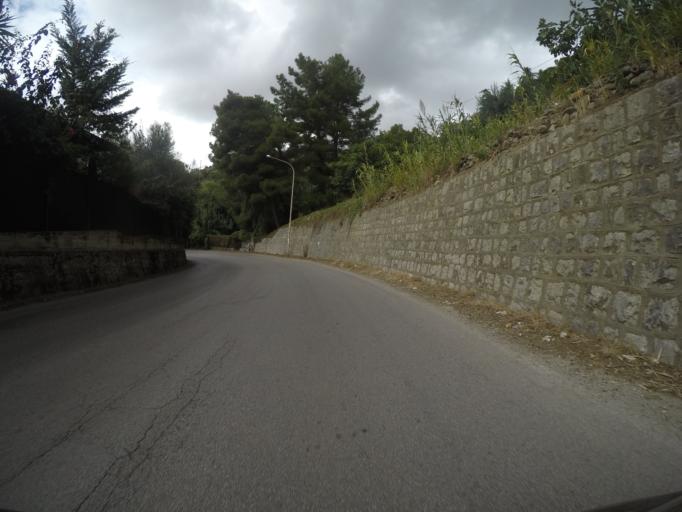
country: IT
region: Sicily
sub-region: Palermo
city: Montelepre
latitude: 38.0942
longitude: 13.1667
